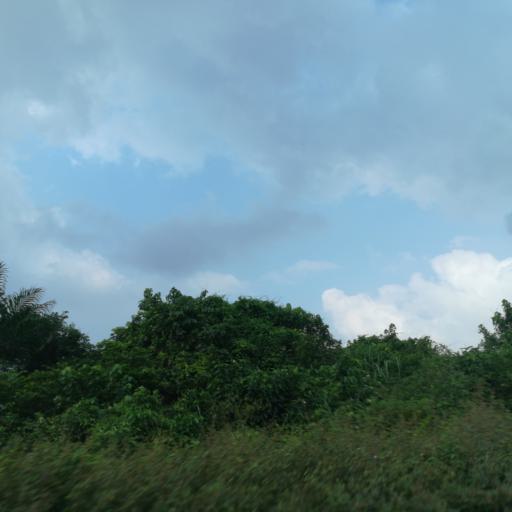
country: NG
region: Rivers
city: Okrika
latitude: 4.8227
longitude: 7.1252
